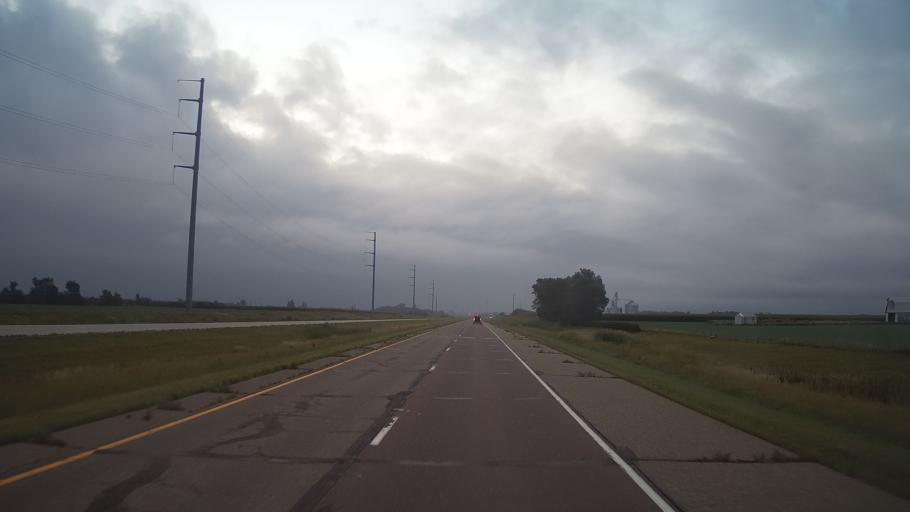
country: US
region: Minnesota
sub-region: Jackson County
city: Lakefield
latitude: 43.6374
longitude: -95.3493
